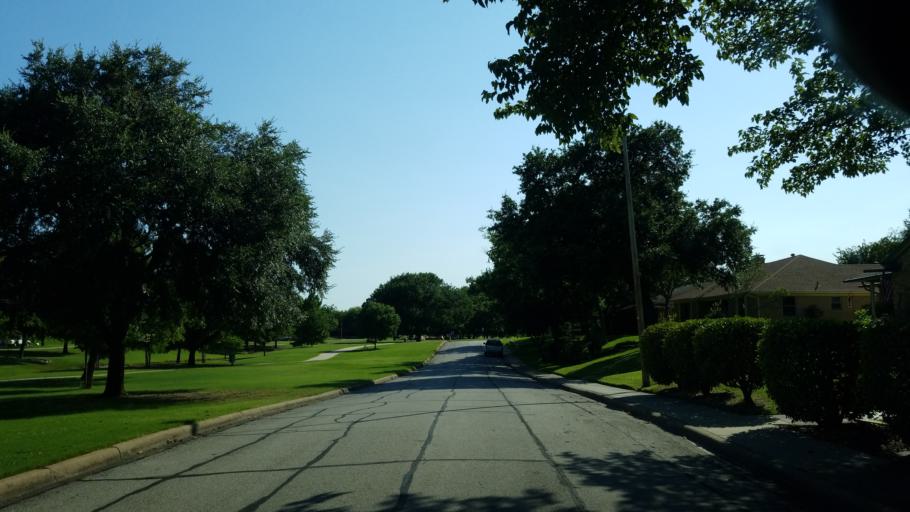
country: US
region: Texas
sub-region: Dallas County
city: Farmers Branch
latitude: 32.9276
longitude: -96.8831
